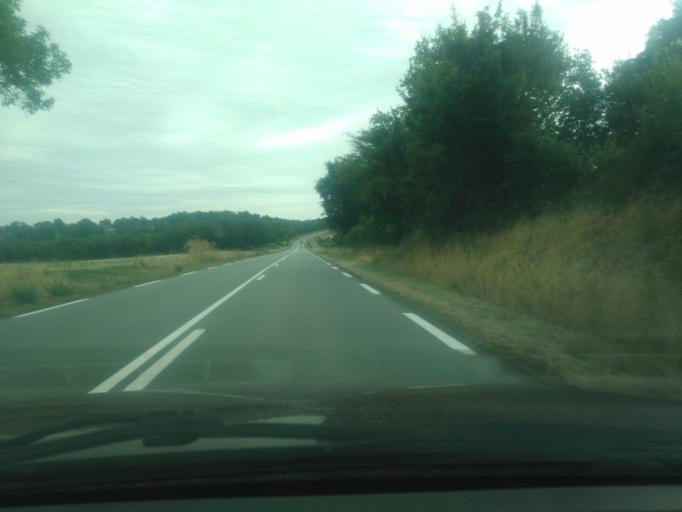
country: FR
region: Centre
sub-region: Departement de l'Indre
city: Neuvy-Saint-Sepulchre
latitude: 46.5792
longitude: 1.8413
